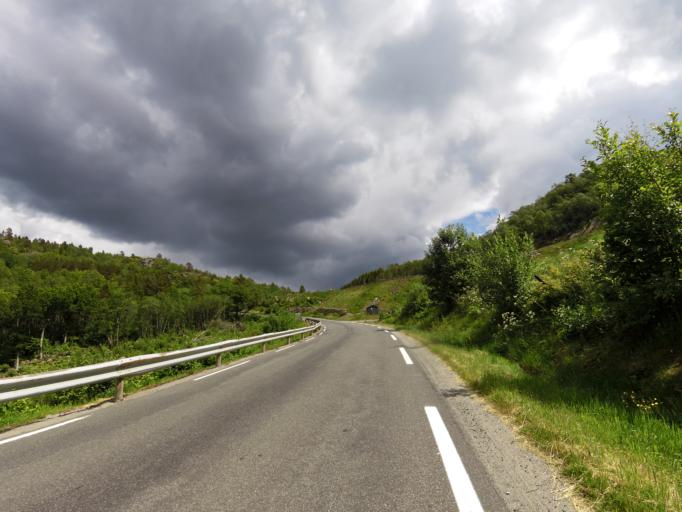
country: NO
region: Vest-Agder
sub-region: Lyngdal
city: Lyngdal
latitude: 58.1150
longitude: 7.0633
